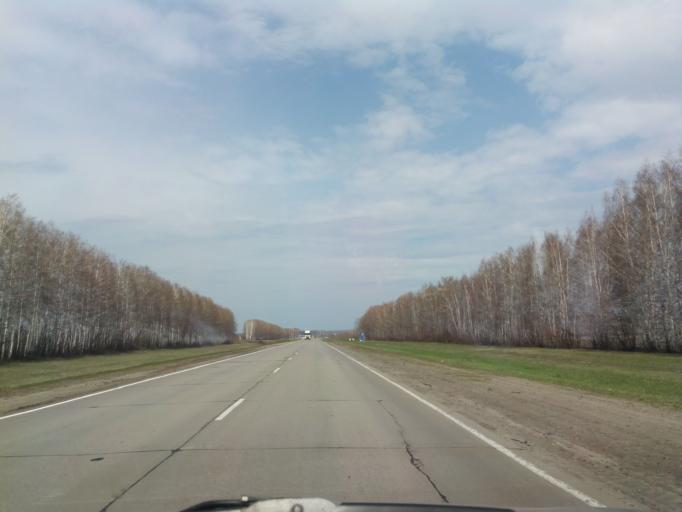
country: RU
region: Tambov
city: Zherdevka
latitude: 52.0692
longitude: 41.6630
